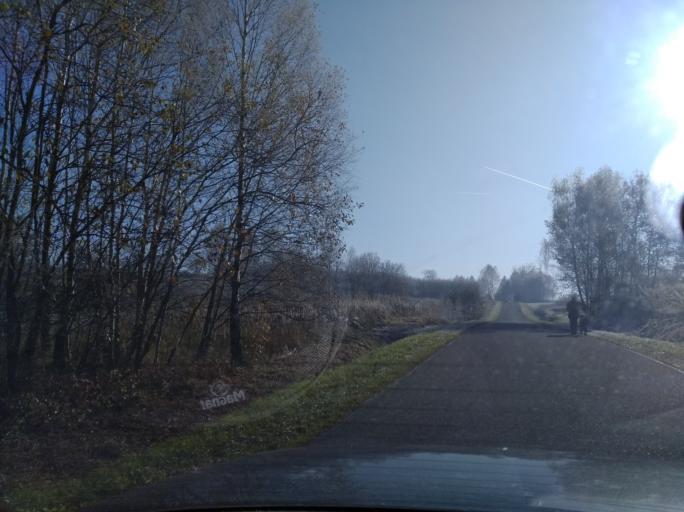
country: PL
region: Subcarpathian Voivodeship
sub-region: Powiat strzyzowski
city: Wysoka Strzyzowska
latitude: 49.8405
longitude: 21.7088
